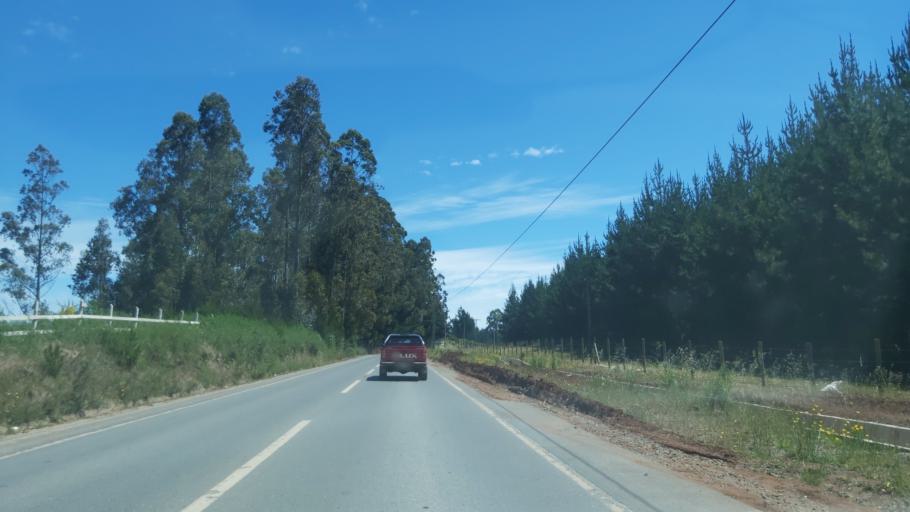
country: CL
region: Maule
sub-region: Provincia de Talca
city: Constitucion
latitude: -35.3960
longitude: -72.4303
